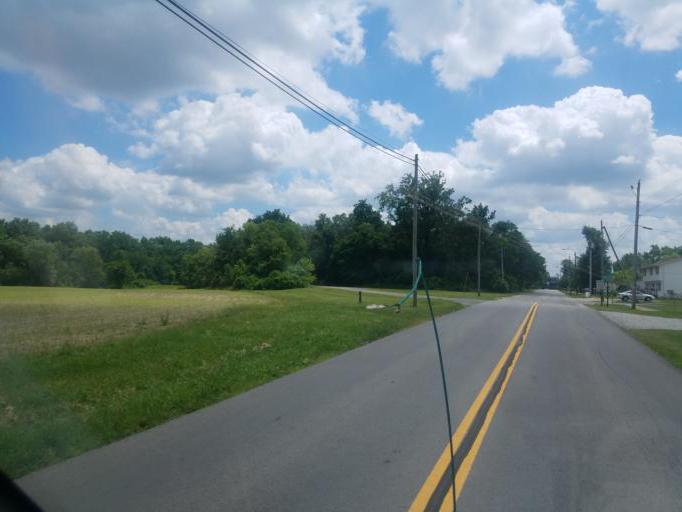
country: US
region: Ohio
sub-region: Huron County
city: Willard
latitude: 41.0665
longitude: -82.7333
